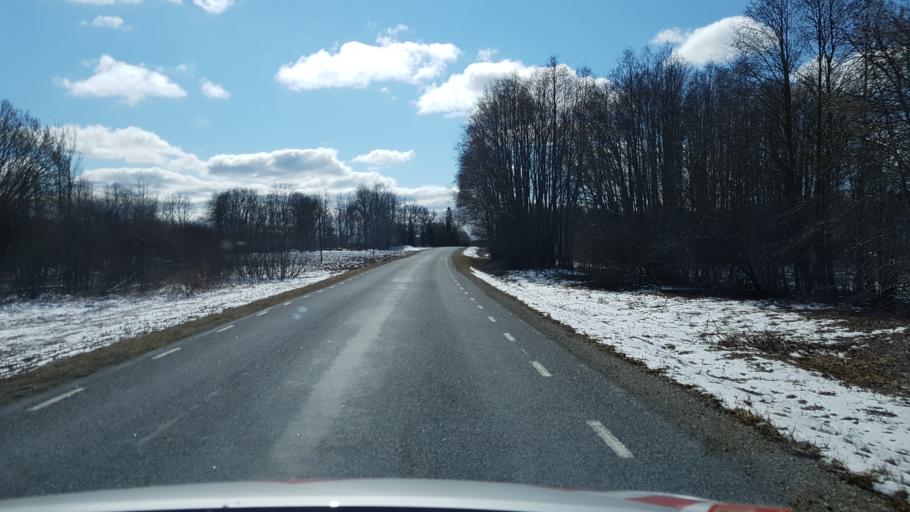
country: EE
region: Laeaene-Virumaa
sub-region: Kadrina vald
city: Kadrina
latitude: 59.4727
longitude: 25.9976
